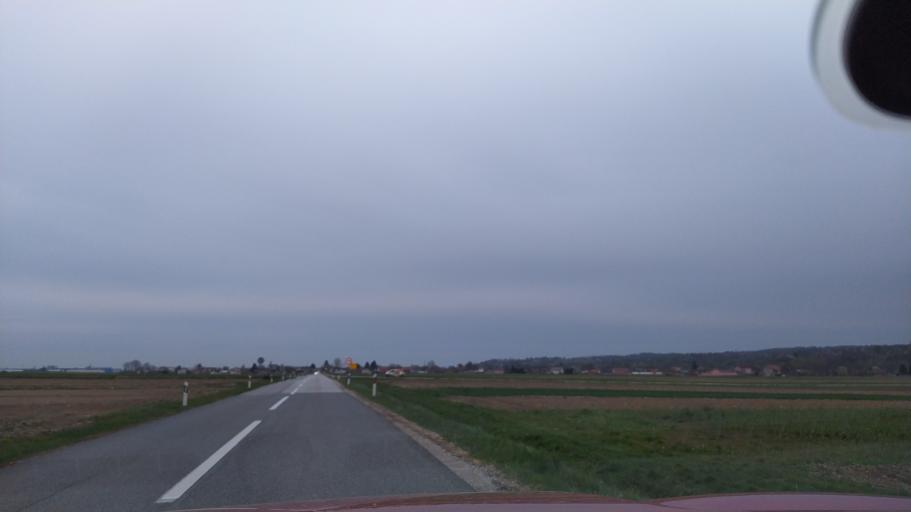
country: HR
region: Varazdinska
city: Ludbreg
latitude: 46.2504
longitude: 16.5722
